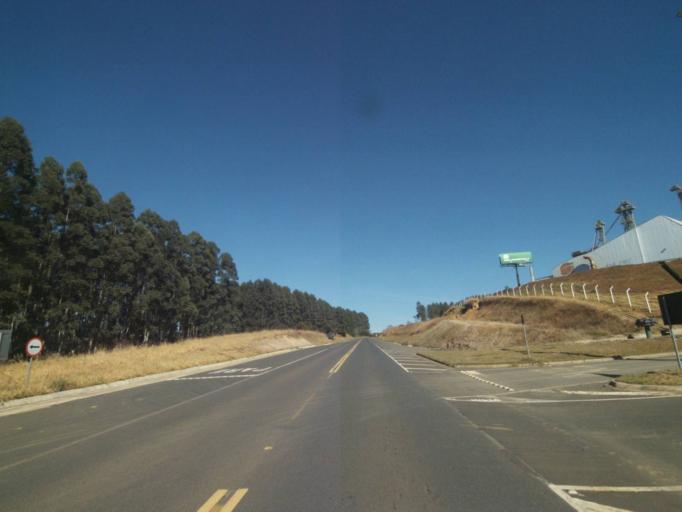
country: BR
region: Parana
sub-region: Tibagi
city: Tibagi
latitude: -24.5209
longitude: -50.4383
